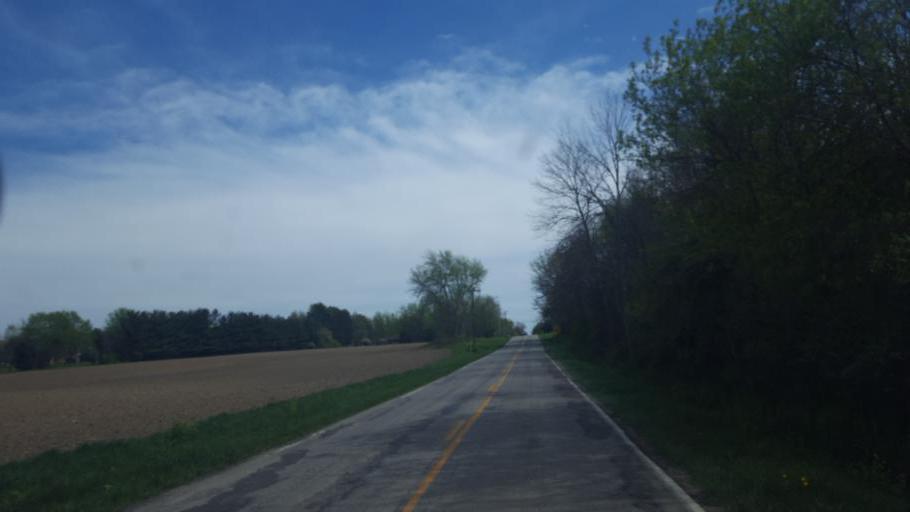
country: US
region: Ohio
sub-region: Richland County
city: Shelby
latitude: 40.8454
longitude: -82.6042
